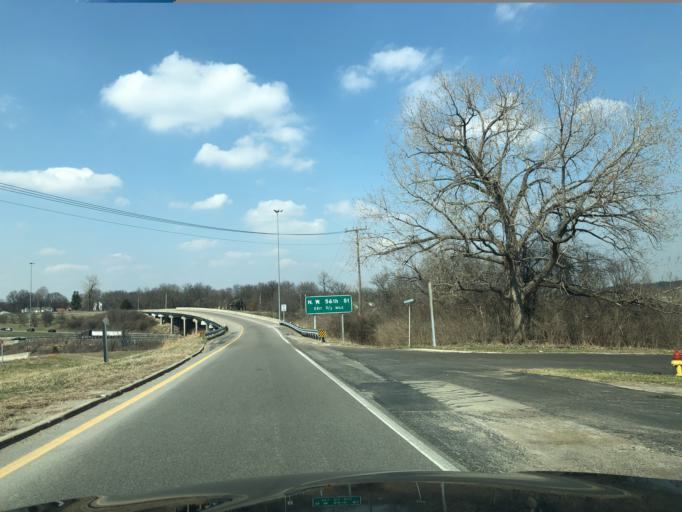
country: US
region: Missouri
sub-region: Platte County
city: Riverside
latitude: 39.1886
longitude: -94.6133
